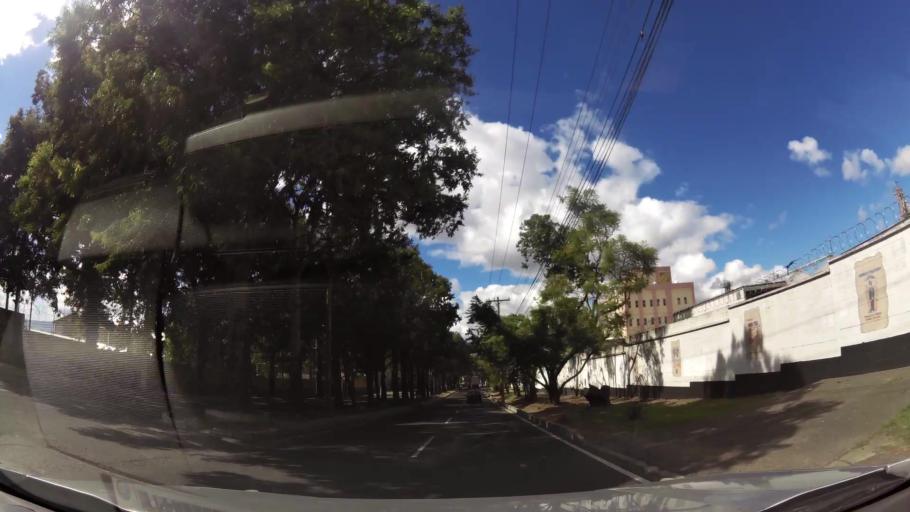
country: GT
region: Guatemala
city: Villa Nueva
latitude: 14.5572
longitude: -90.5497
